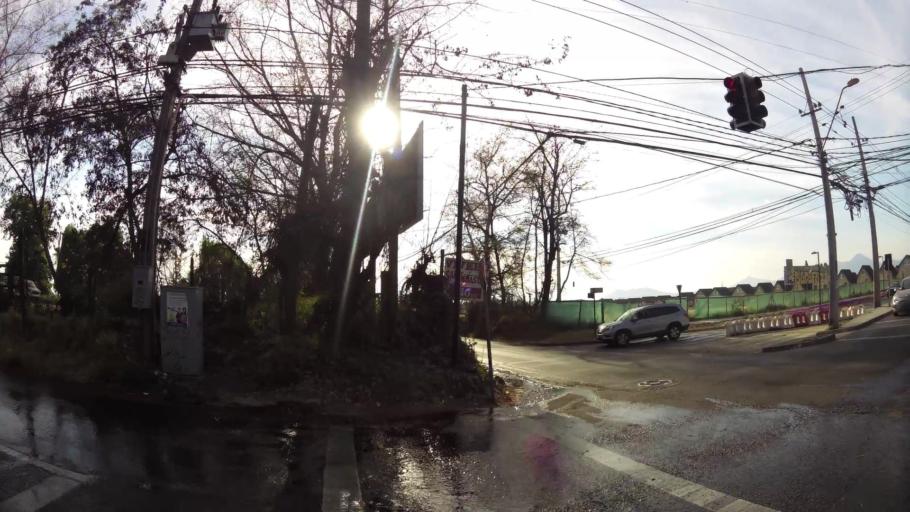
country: CL
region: Santiago Metropolitan
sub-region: Provincia de Santiago
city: Villa Presidente Frei, Nunoa, Santiago, Chile
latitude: -33.5001
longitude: -70.5523
